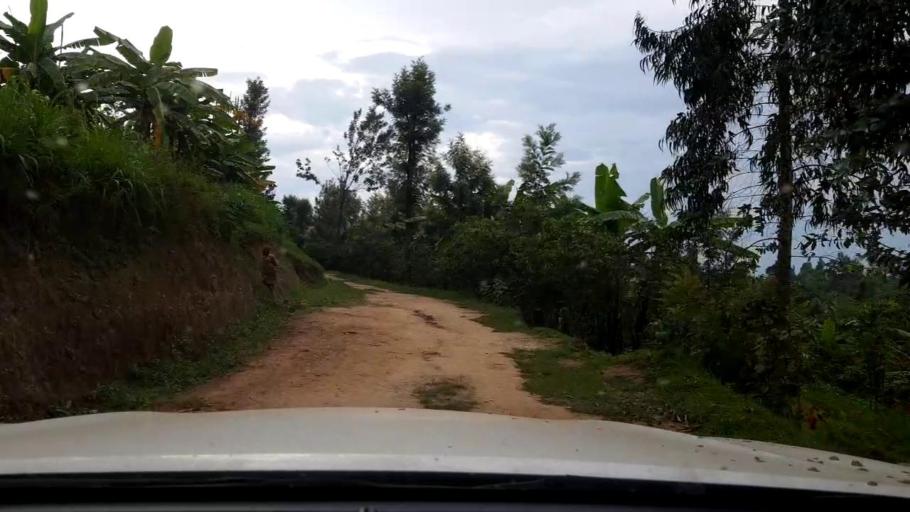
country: RW
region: Western Province
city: Kibuye
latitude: -2.0009
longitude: 29.3712
